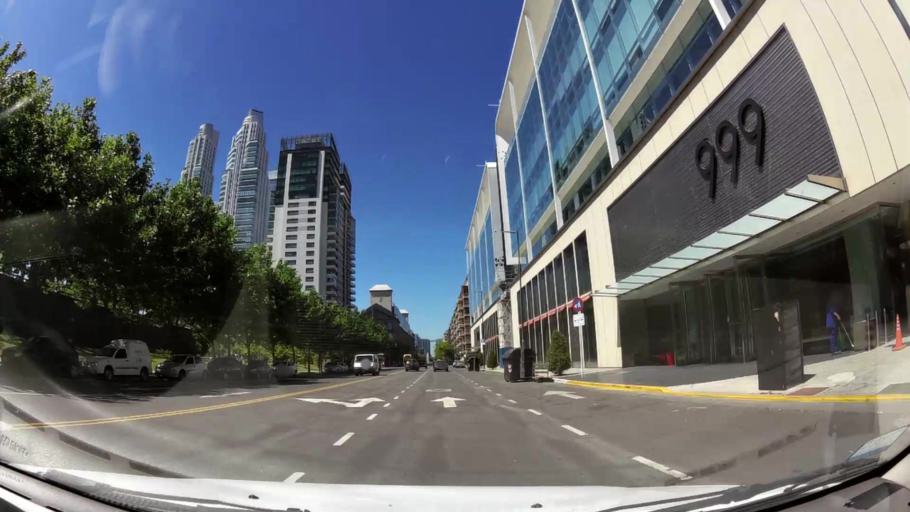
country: AR
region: Buenos Aires F.D.
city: Buenos Aires
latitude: -34.6083
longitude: -58.3630
